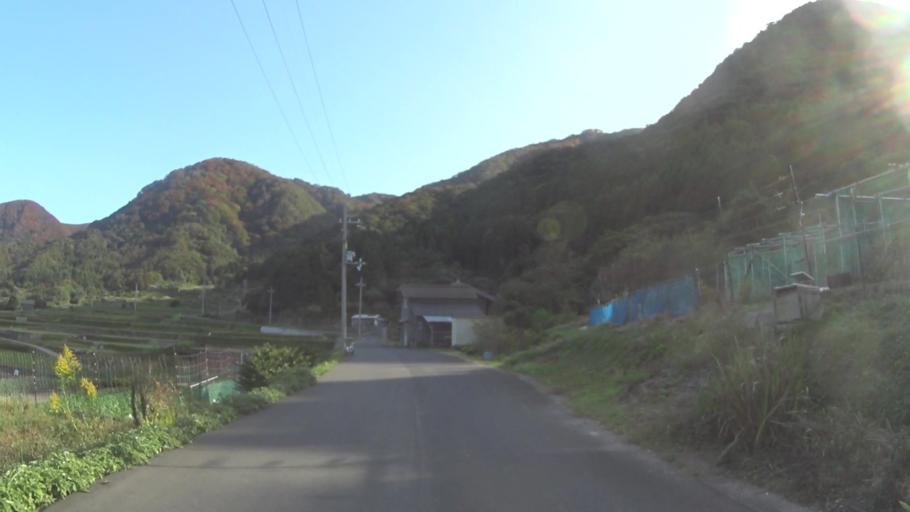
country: JP
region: Kyoto
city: Miyazu
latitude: 35.7628
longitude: 135.1999
